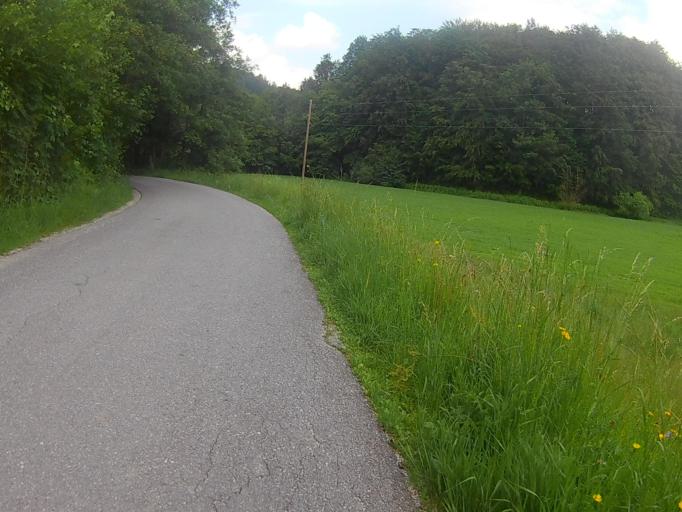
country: SI
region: Maribor
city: Kamnica
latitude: 46.6002
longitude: 15.5946
